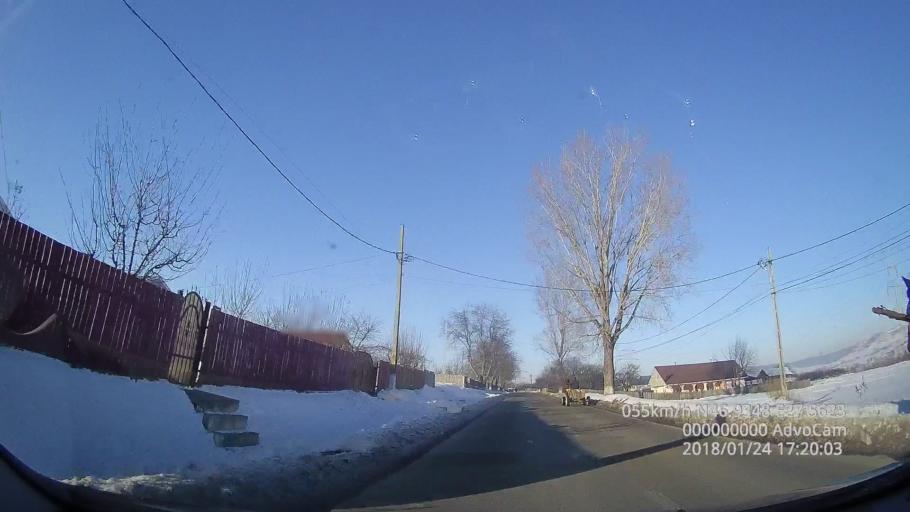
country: RO
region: Iasi
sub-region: Comuna Scanteia
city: Scanteia
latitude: 46.9352
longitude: 27.5623
